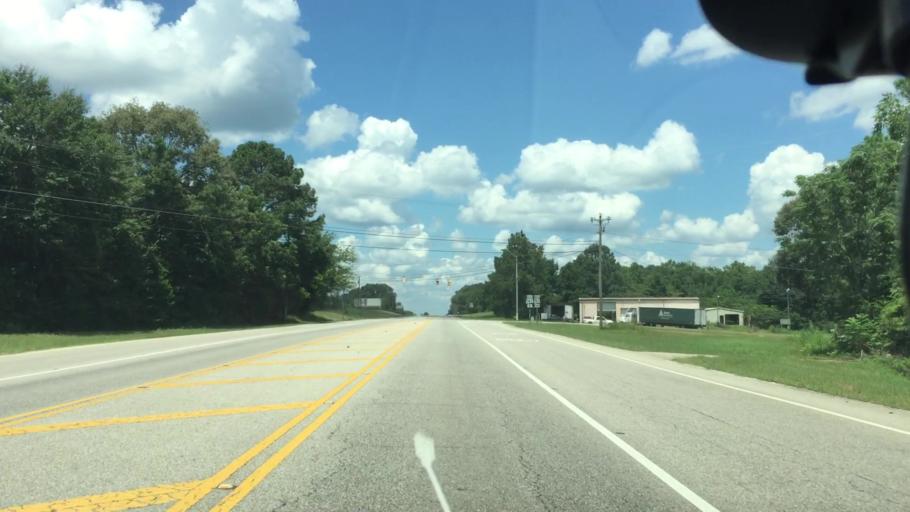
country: US
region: Alabama
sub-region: Coffee County
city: New Brockton
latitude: 31.4262
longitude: -85.8881
